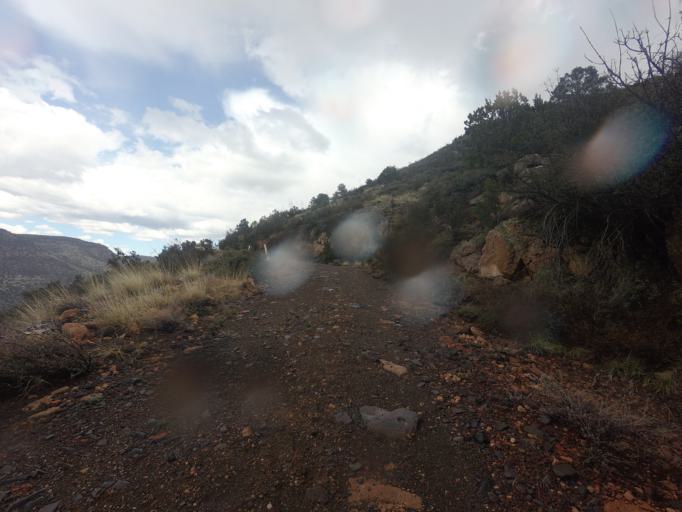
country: US
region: Arizona
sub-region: Gila County
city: Pine
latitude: 34.4065
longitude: -111.5918
